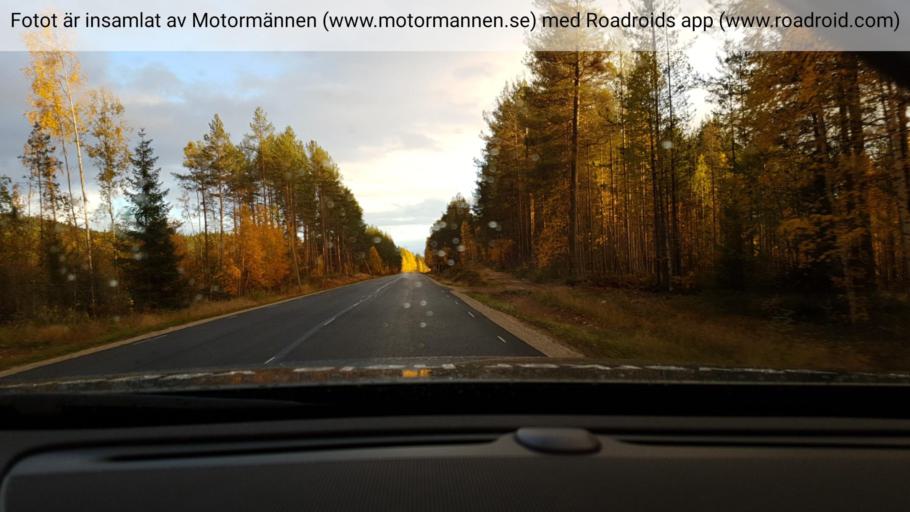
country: SE
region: Norrbotten
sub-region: Overkalix Kommun
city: OEverkalix
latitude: 66.4394
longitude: 22.7898
